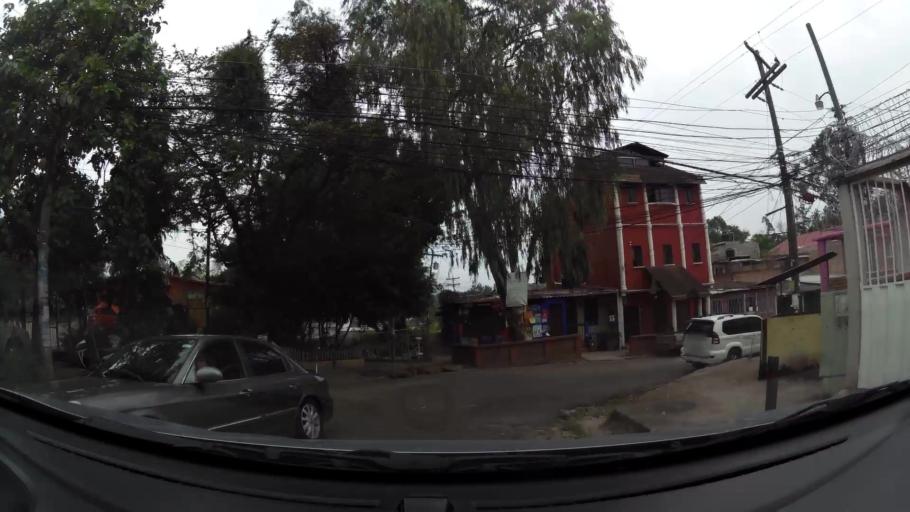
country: HN
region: Francisco Morazan
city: Tegucigalpa
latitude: 14.0723
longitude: -87.1747
